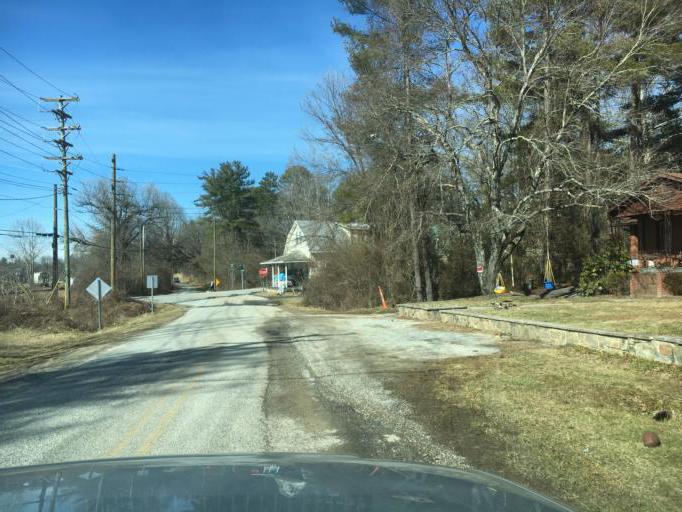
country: US
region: North Carolina
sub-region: Henderson County
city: Mountain Home
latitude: 35.3926
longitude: -82.5005
